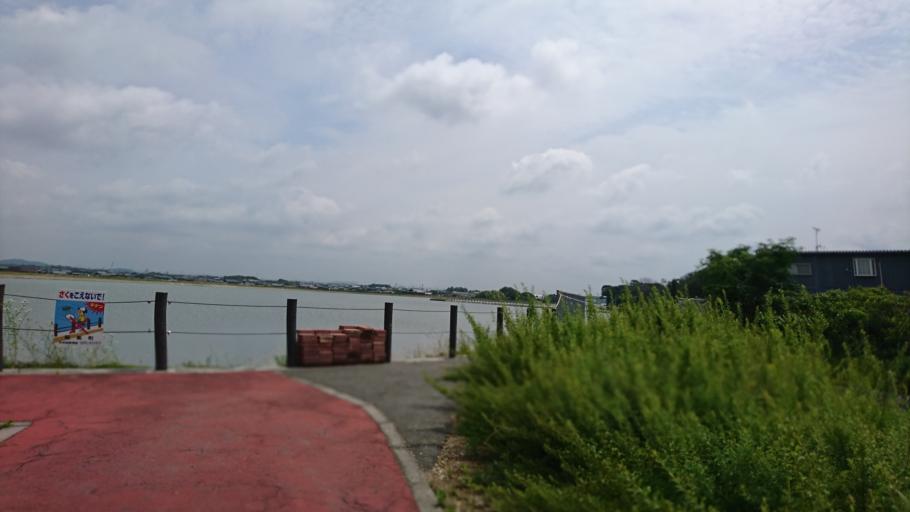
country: JP
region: Hyogo
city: Miki
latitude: 34.7536
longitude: 134.9207
